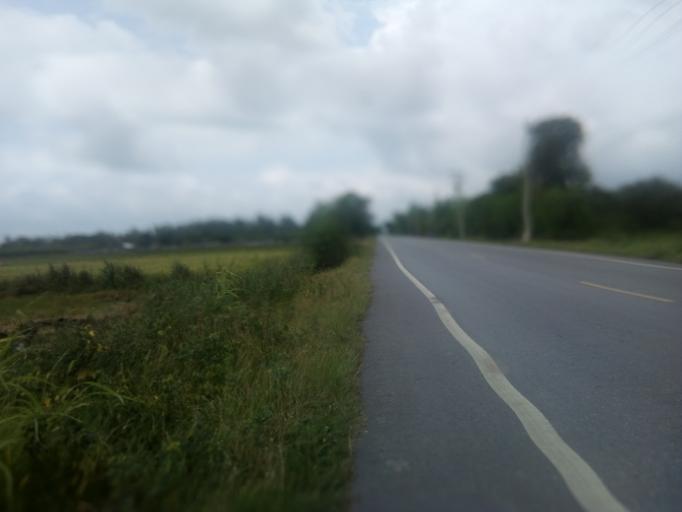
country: TH
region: Pathum Thani
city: Ban Lam Luk Ka
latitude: 13.9976
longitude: 100.8218
